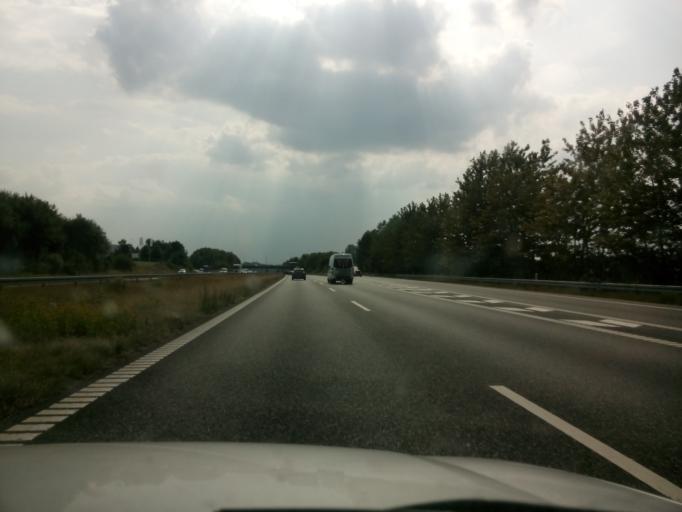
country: DK
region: Central Jutland
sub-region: Skanderborg Kommune
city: Stilling
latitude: 56.0693
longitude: 9.9835
